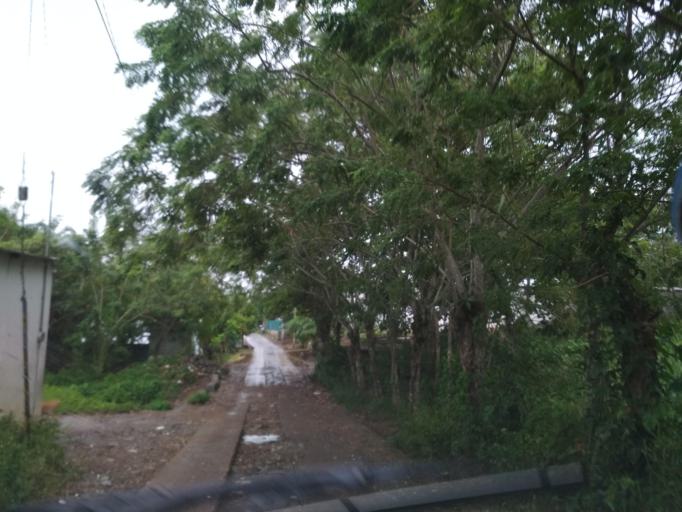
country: MX
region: Veracruz
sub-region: San Andres Tuxtla
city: Soyata
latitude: 18.4125
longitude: -95.2989
